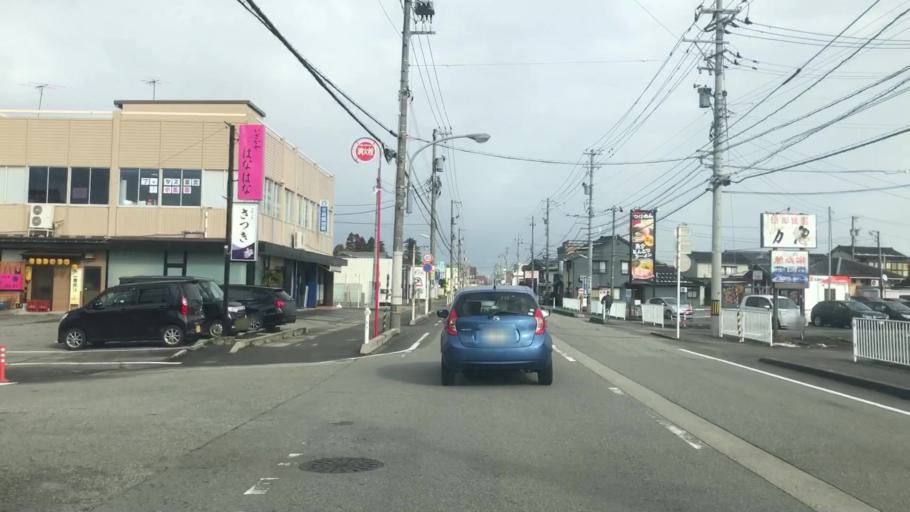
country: JP
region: Toyama
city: Toyama-shi
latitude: 36.6574
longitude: 137.2188
